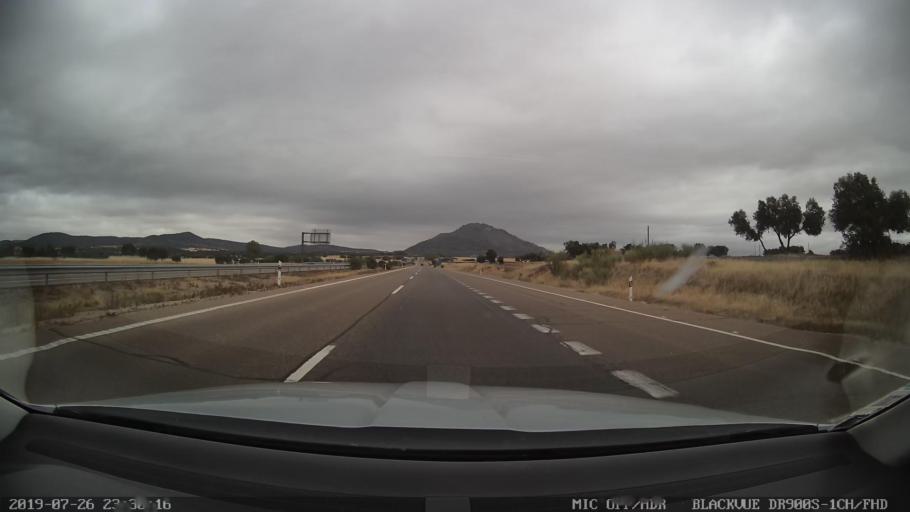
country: ES
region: Extremadura
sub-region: Provincia de Caceres
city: Villamesias
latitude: 39.2760
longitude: -5.8561
